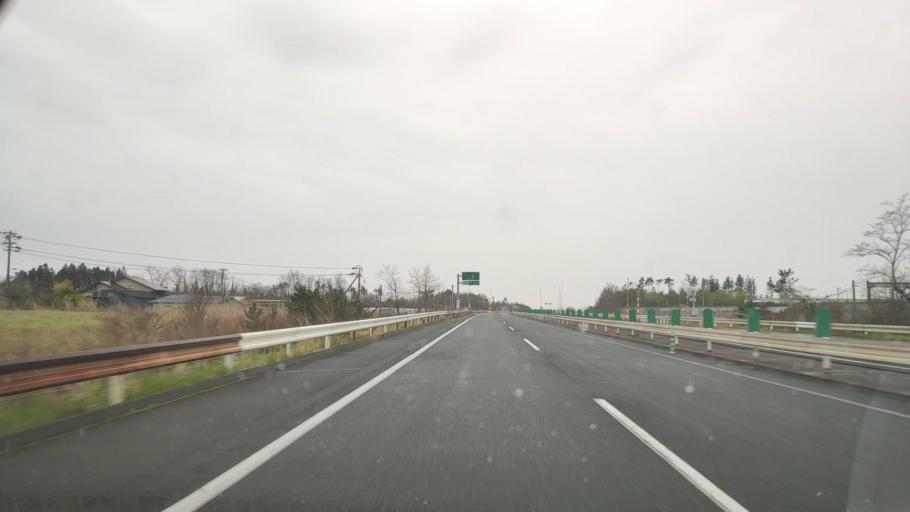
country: JP
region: Akita
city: Noshiromachi
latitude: 40.1233
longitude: 140.0122
